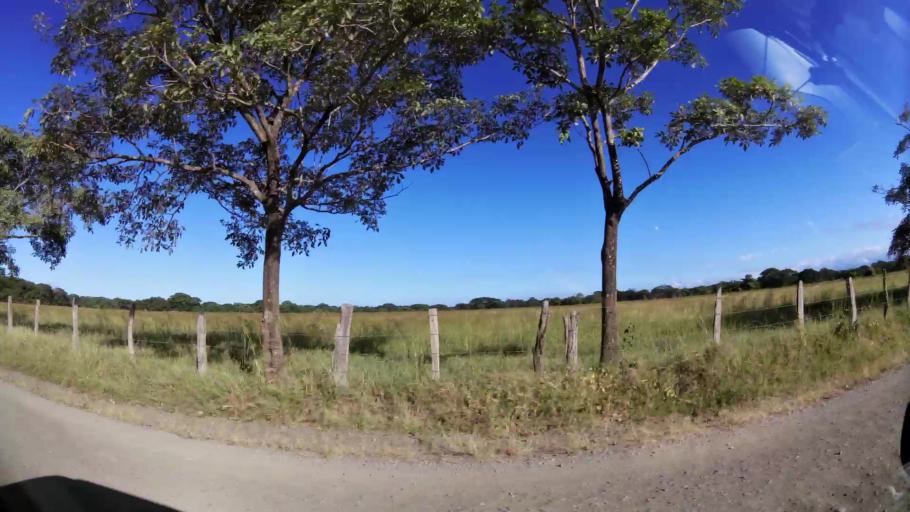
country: CR
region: Guanacaste
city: Sardinal
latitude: 10.4831
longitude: -85.5929
